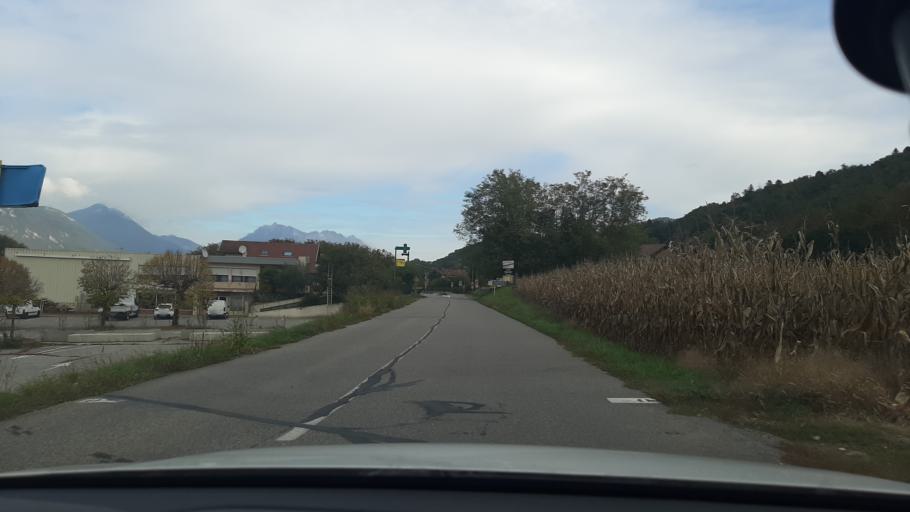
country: FR
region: Rhone-Alpes
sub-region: Departement de l'Isere
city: Pontcharra
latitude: 45.4439
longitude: 6.0337
